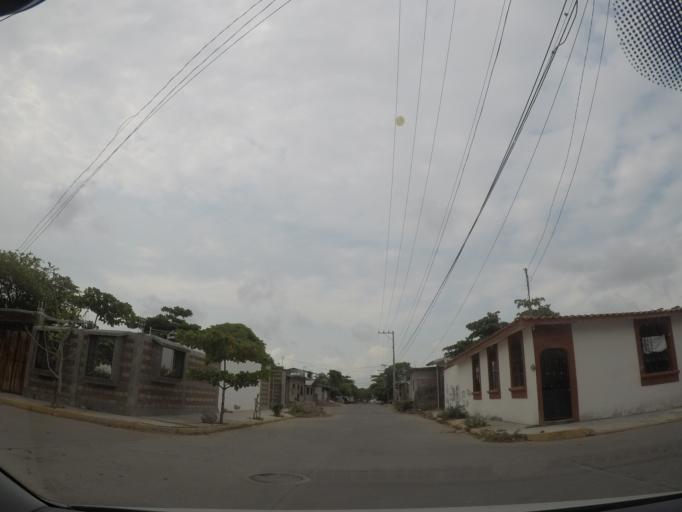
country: MX
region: Oaxaca
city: Juchitan de Zaragoza
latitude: 16.4540
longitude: -95.0156
